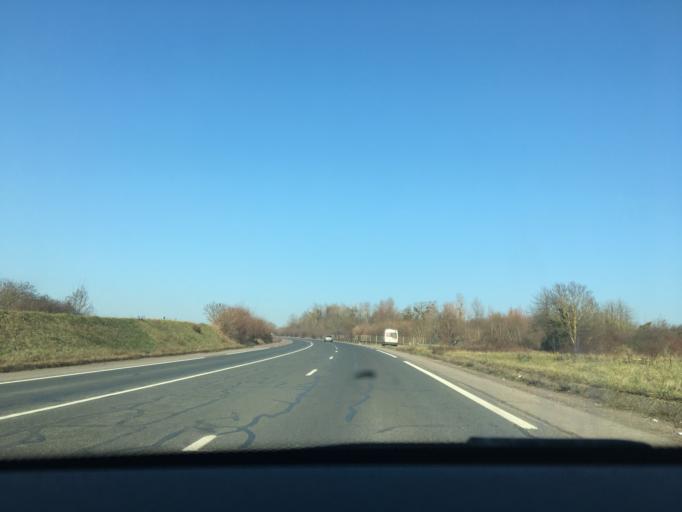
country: FR
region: Ile-de-France
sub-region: Departement des Yvelines
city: Limay
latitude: 48.9976
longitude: 1.7504
